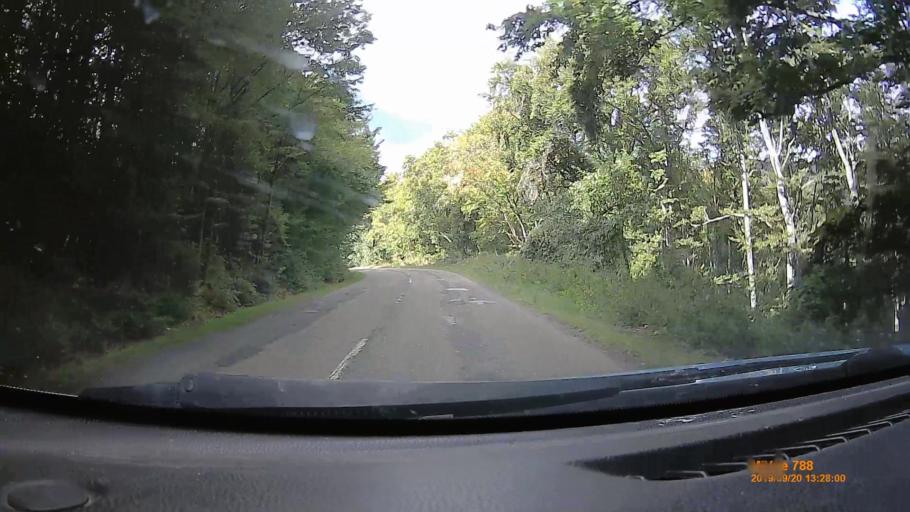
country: HU
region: Heves
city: Szilvasvarad
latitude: 48.0449
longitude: 20.4903
